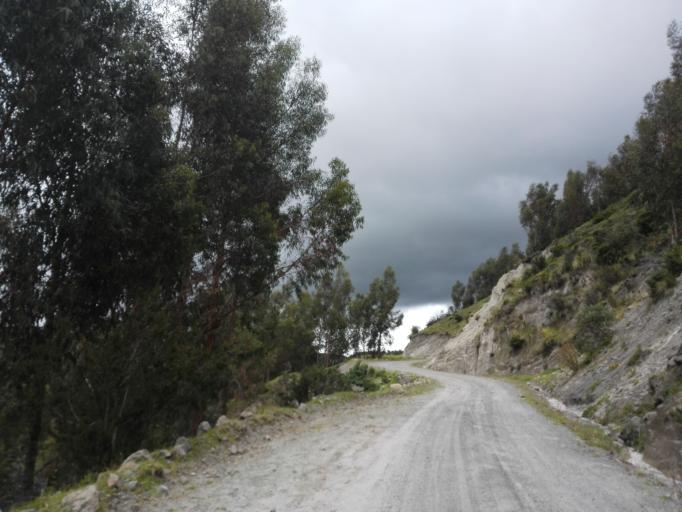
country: PE
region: Ayacucho
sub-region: Provincia de Huamanga
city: Vinchos
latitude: -13.3223
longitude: -74.4404
